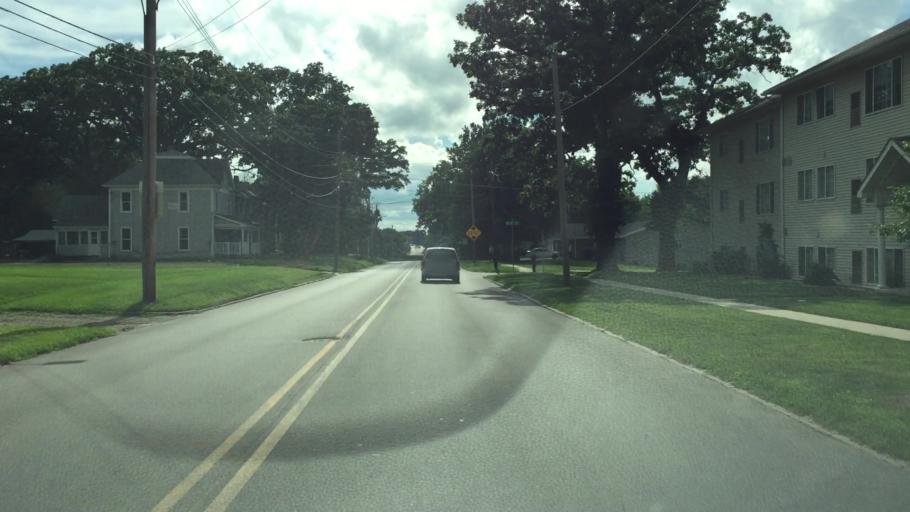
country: US
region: Iowa
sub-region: Jasper County
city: Newton
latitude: 41.6995
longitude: -93.0644
